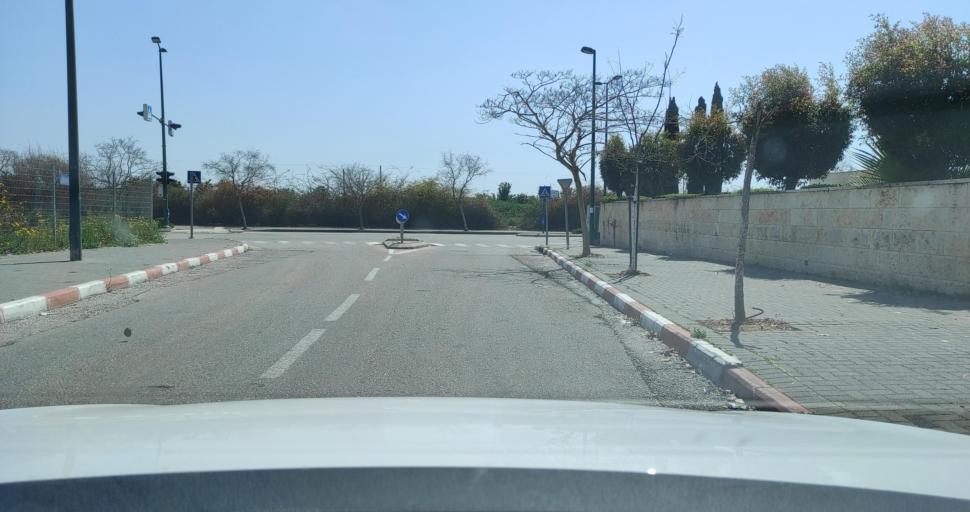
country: IL
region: Central District
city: Even Yehuda
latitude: 32.2954
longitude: 34.8713
